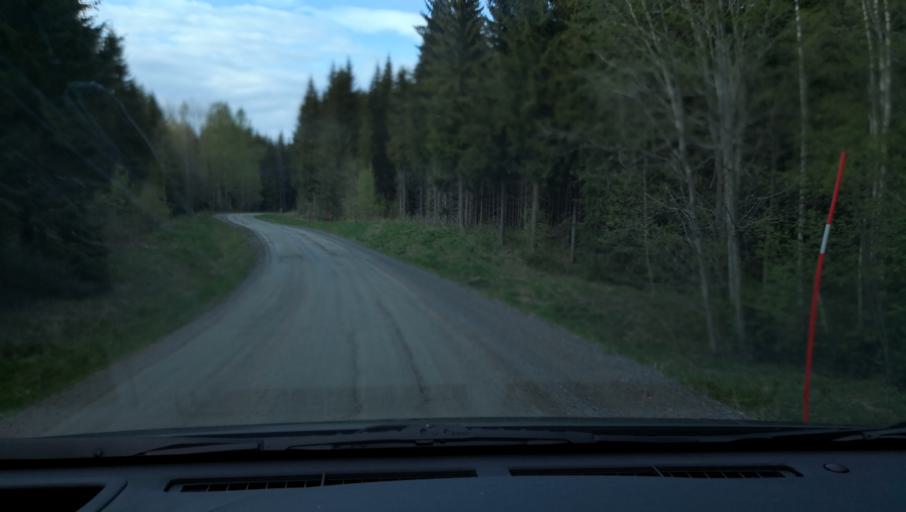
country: SE
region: Dalarna
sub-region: Saters Kommun
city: Saeter
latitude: 60.2669
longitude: 15.8273
